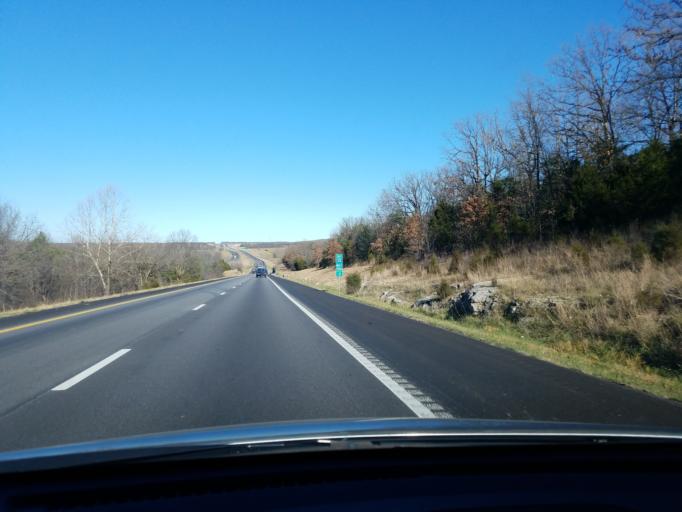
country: US
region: Missouri
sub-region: Webster County
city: Marshfield
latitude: 37.4063
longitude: -92.8925
